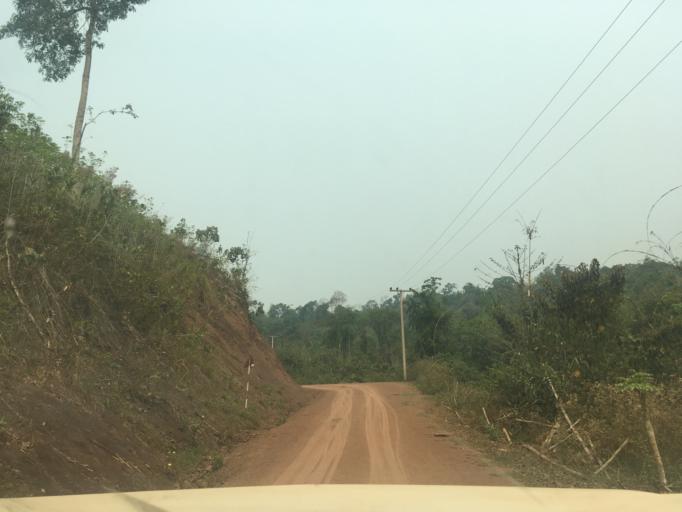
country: VN
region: Huyen Dien Bien
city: Thi Tran Muong Cha
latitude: 21.6856
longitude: 102.8377
